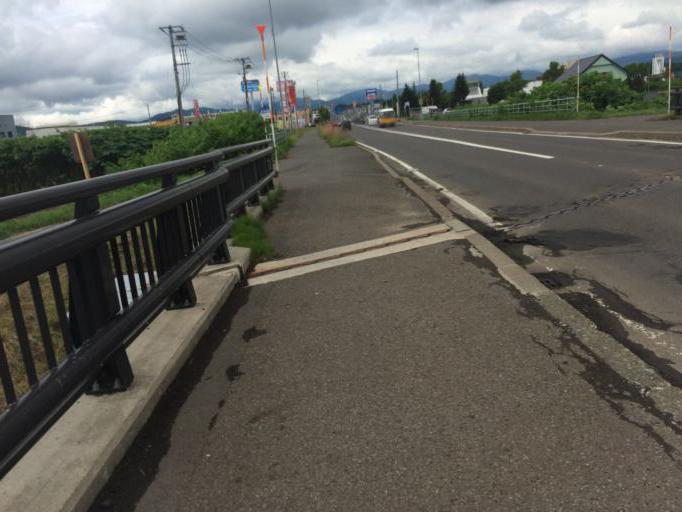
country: JP
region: Hokkaido
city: Niseko Town
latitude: 42.8866
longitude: 140.7512
